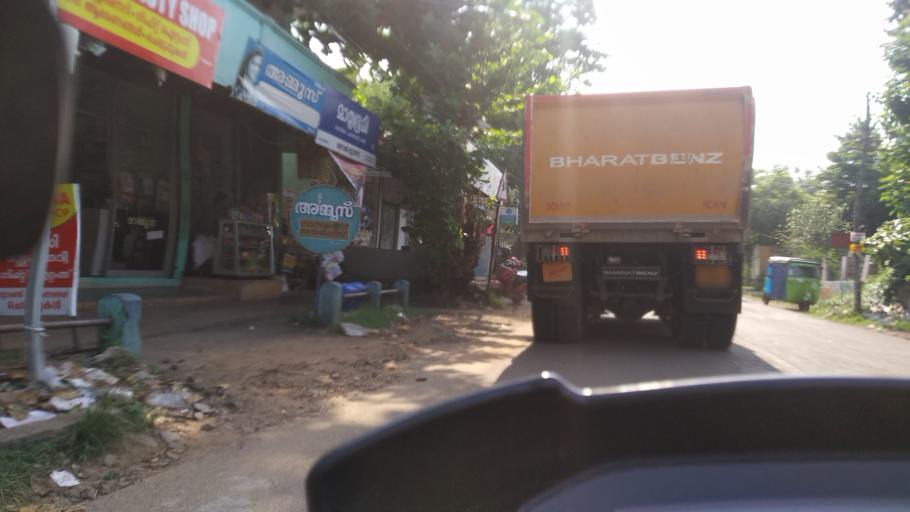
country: IN
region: Kerala
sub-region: Ernakulam
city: Piravam
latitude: 9.8742
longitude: 76.4956
